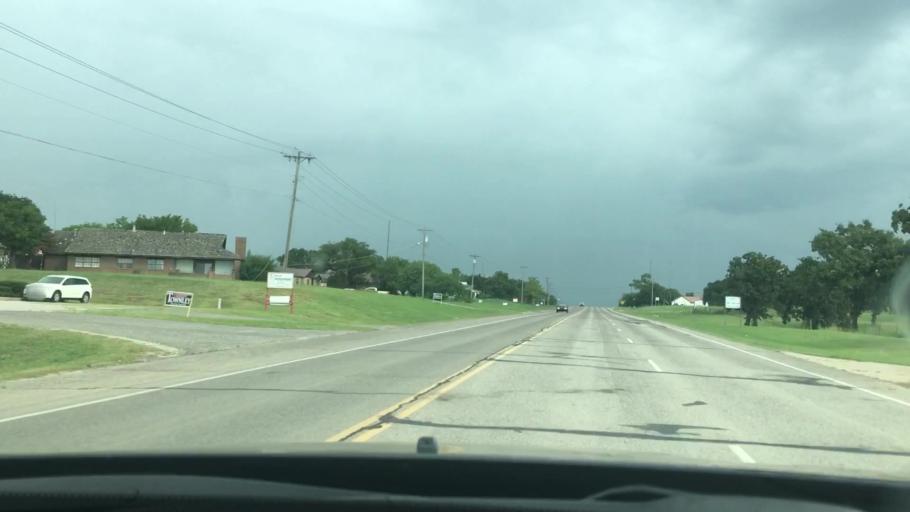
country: US
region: Oklahoma
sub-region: Carter County
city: Healdton
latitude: 34.2133
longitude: -97.4748
